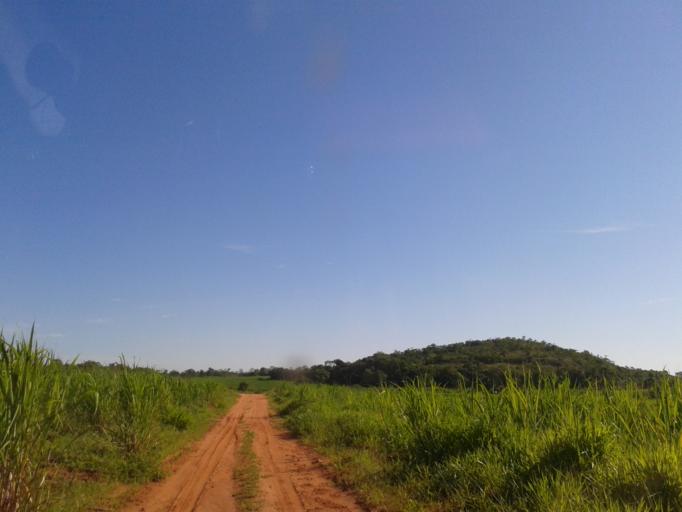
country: BR
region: Minas Gerais
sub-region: Santa Vitoria
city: Santa Vitoria
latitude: -19.1231
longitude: -50.0035
